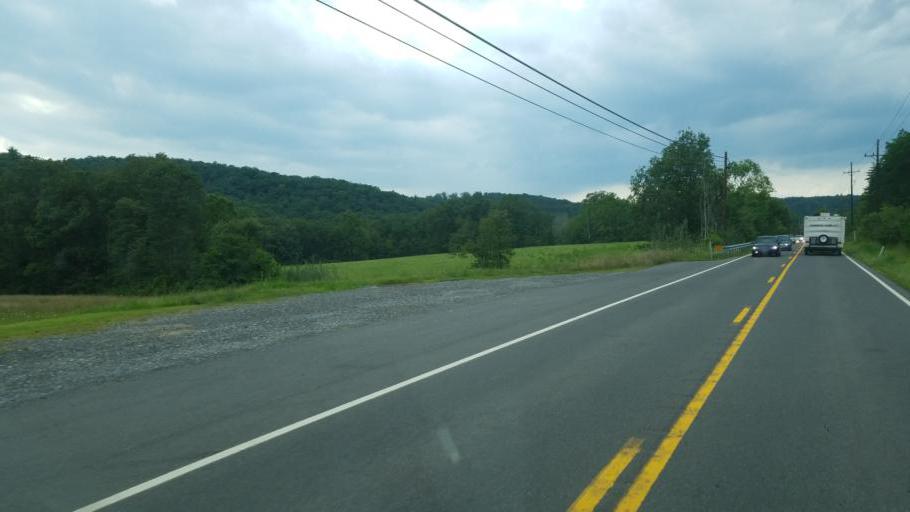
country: US
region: West Virginia
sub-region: Morgan County
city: Berkeley Springs
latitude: 39.5378
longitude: -78.4789
